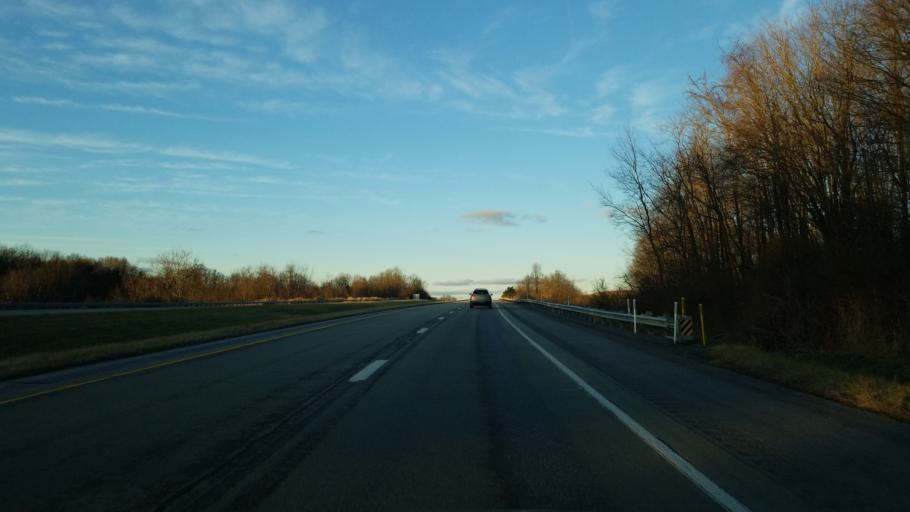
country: US
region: Pennsylvania
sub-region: Indiana County
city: Chevy Chase Heights
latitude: 40.6425
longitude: -79.1174
